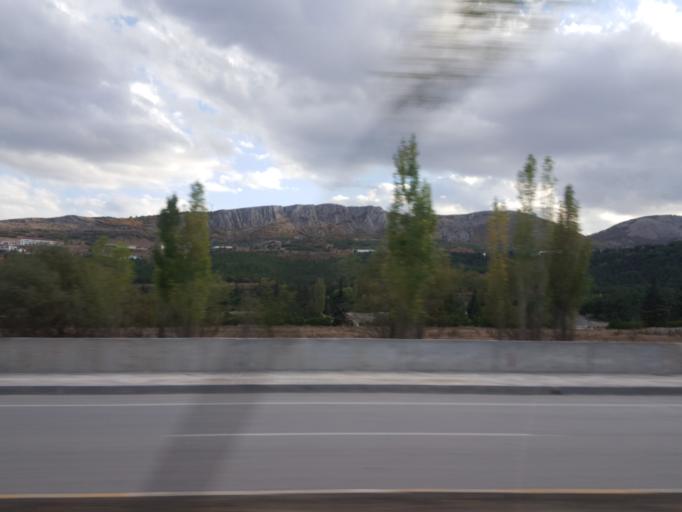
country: TR
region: Tokat
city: Tokat
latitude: 40.3352
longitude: 36.5090
